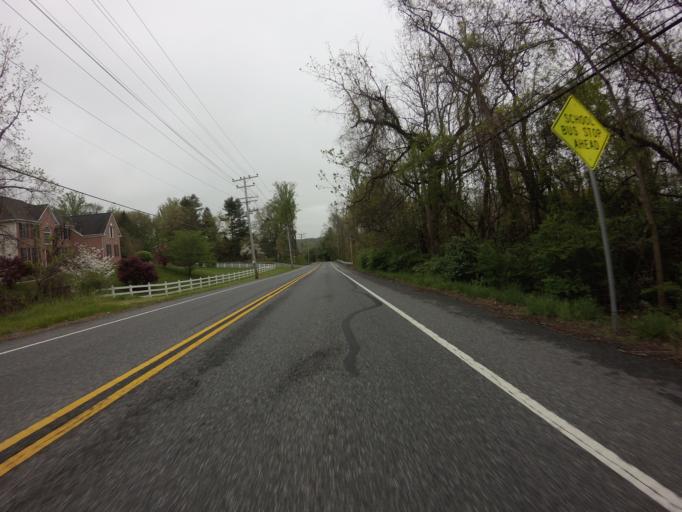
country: US
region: Maryland
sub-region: Baltimore County
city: Hunt Valley
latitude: 39.5548
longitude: -76.6539
